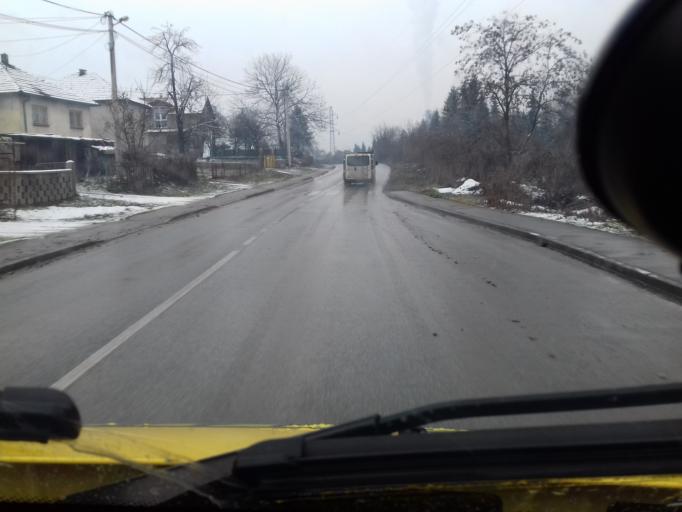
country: BA
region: Federation of Bosnia and Herzegovina
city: Zenica
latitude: 44.2248
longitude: 17.8919
